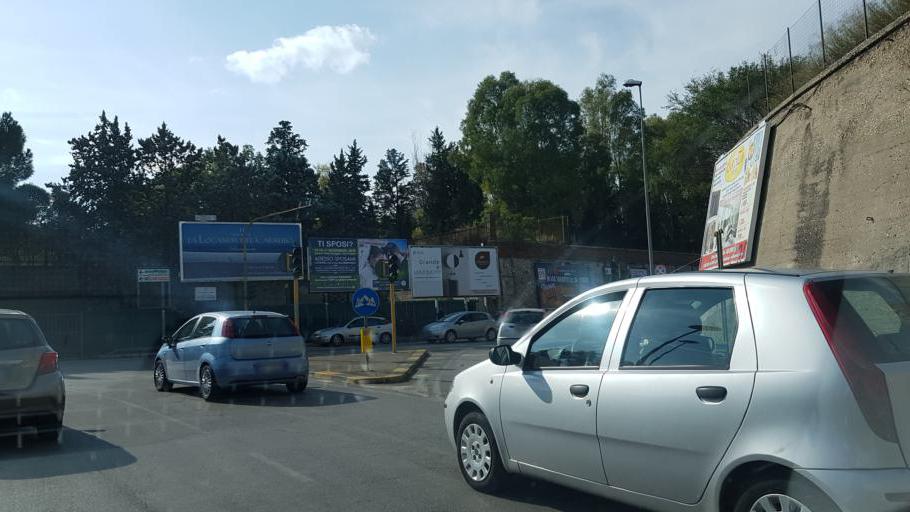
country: IT
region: Apulia
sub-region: Provincia di Foggia
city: Foggia
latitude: 41.4626
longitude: 15.5631
